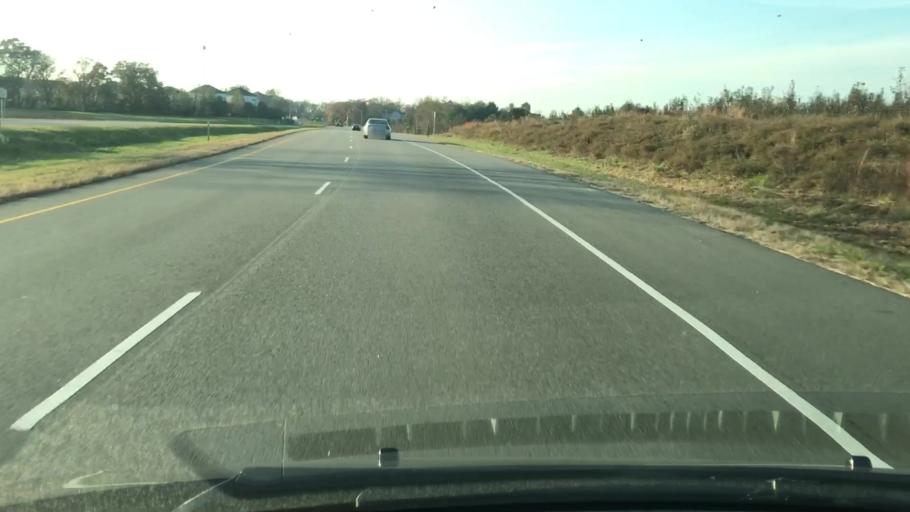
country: US
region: Virginia
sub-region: Fairfax County
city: Lorton
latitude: 38.7063
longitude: -77.2503
